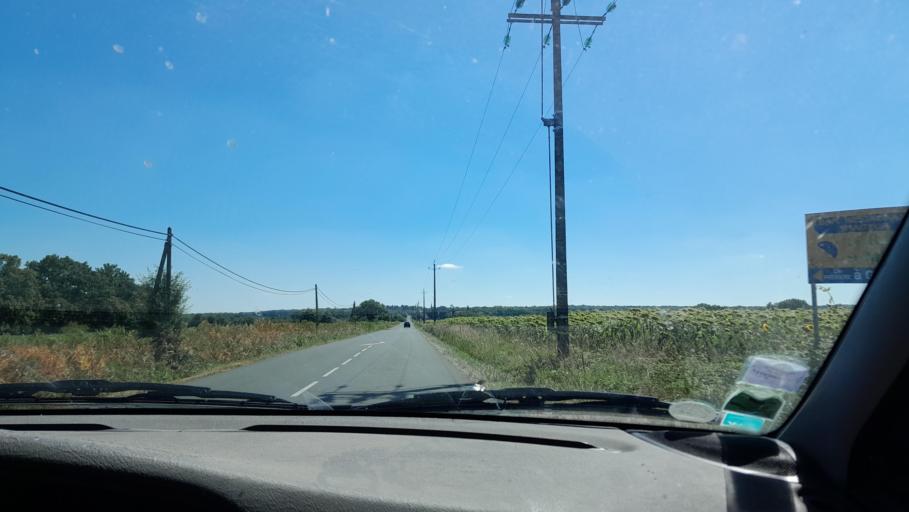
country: FR
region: Pays de la Loire
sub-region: Departement de Maine-et-Loire
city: Pouance
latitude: 47.7300
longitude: -1.1777
